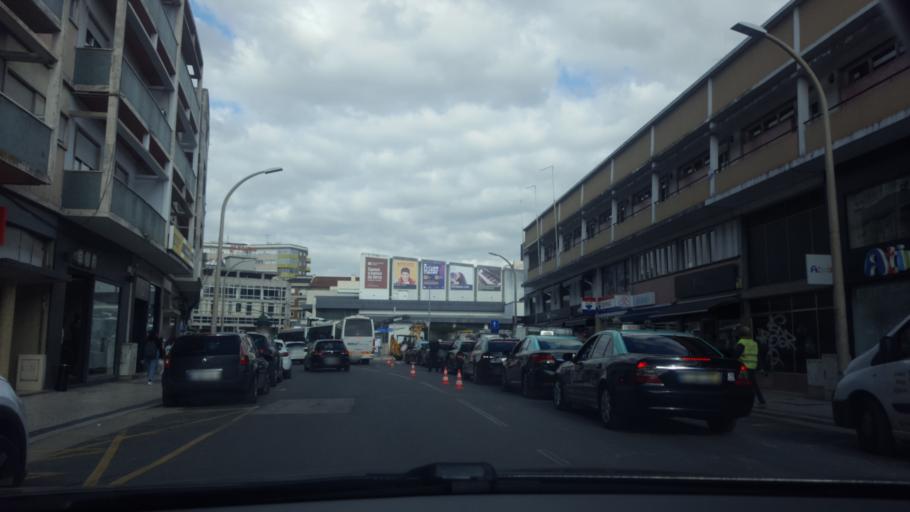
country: PT
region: Leiria
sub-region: Leiria
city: Leiria
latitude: 39.7458
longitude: -8.8049
